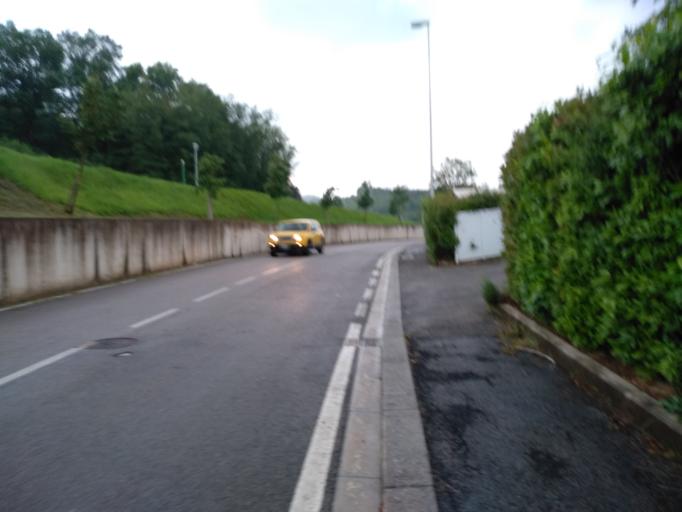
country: IT
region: Tuscany
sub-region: Province of Arezzo
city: San Giovanni Valdarno
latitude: 43.5579
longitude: 11.5290
